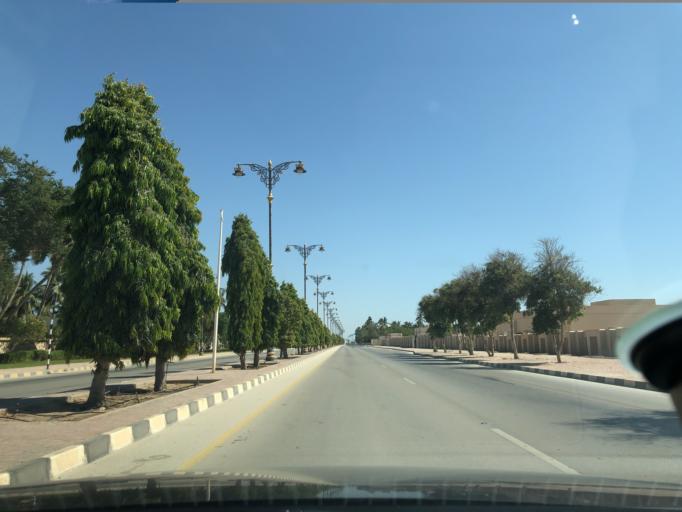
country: OM
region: Zufar
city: Salalah
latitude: 17.0261
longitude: 54.1500
